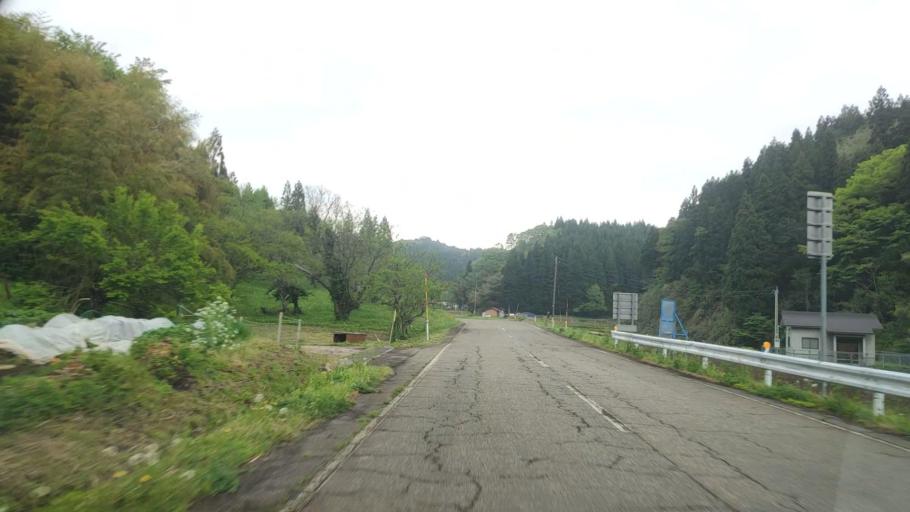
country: JP
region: Niigata
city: Gosen
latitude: 37.7097
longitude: 139.0993
